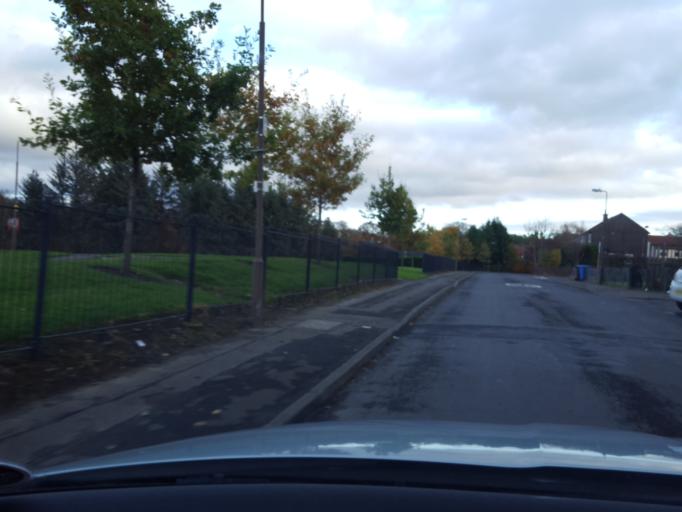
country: GB
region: Scotland
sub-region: West Lothian
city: West Calder
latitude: 55.8598
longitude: -3.5507
